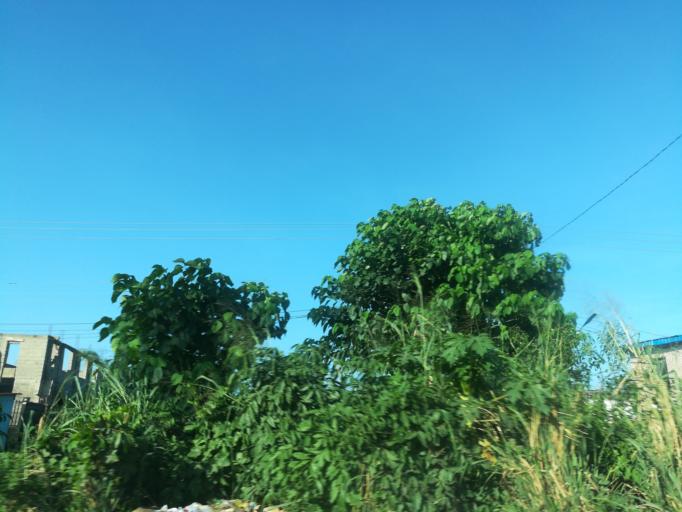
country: NG
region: Lagos
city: Ebute Ikorodu
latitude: 6.5450
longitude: 3.5440
